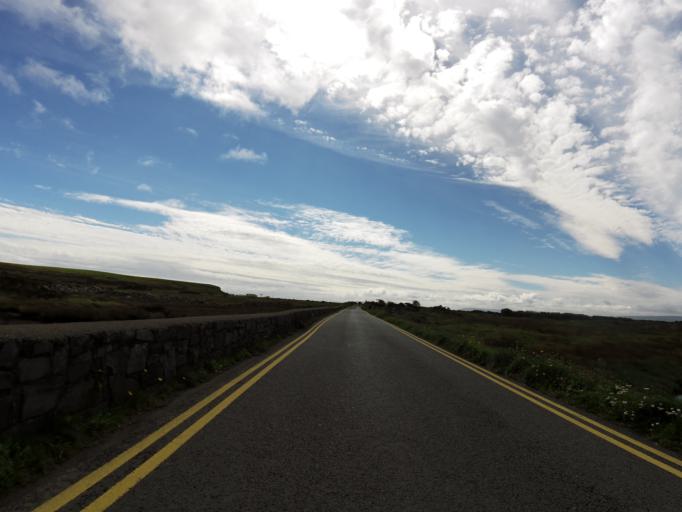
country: IE
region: Connaught
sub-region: County Galway
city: Bearna
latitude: 53.2540
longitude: -9.1301
